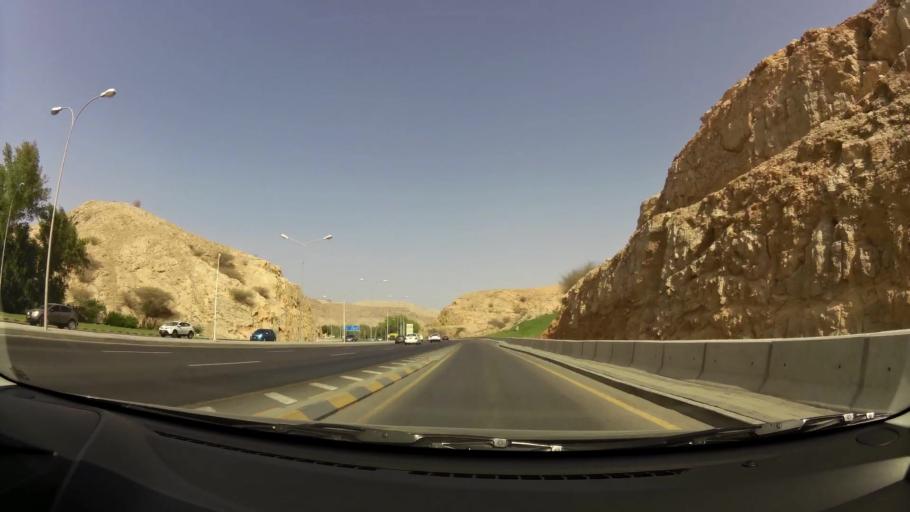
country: OM
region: Muhafazat Masqat
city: Muscat
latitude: 23.6074
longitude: 58.5023
